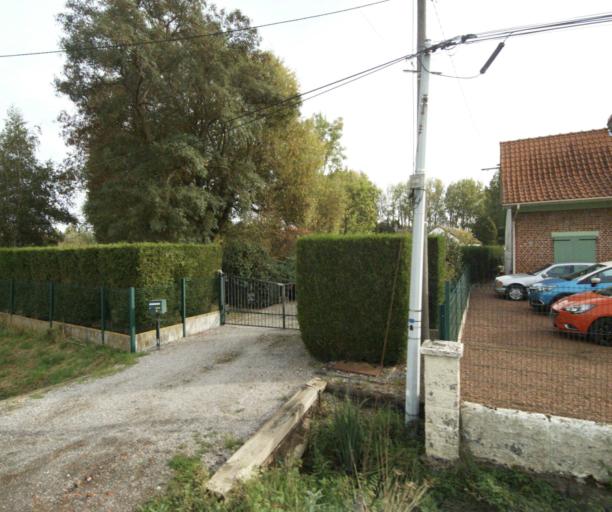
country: FR
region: Nord-Pas-de-Calais
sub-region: Departement du Nord
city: Aubers
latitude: 50.6155
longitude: 2.8507
